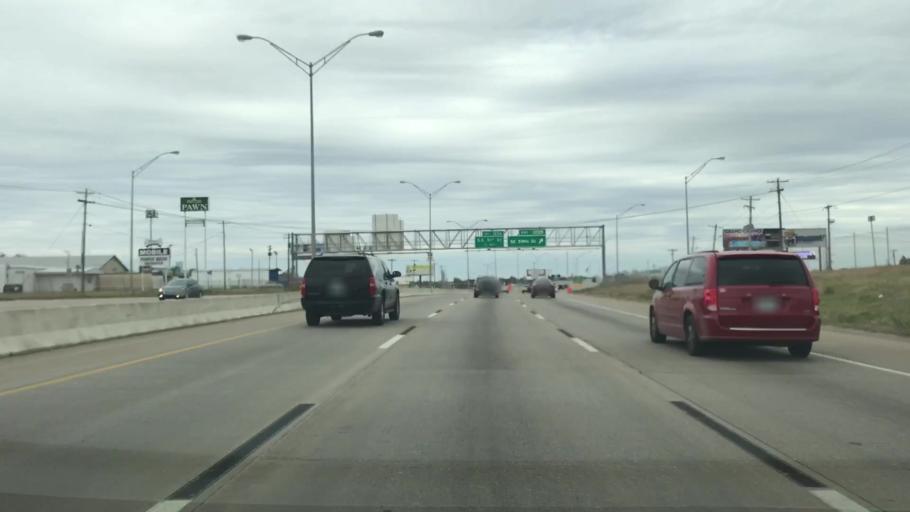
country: US
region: Oklahoma
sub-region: Cleveland County
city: Moore
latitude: 35.4017
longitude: -97.4949
